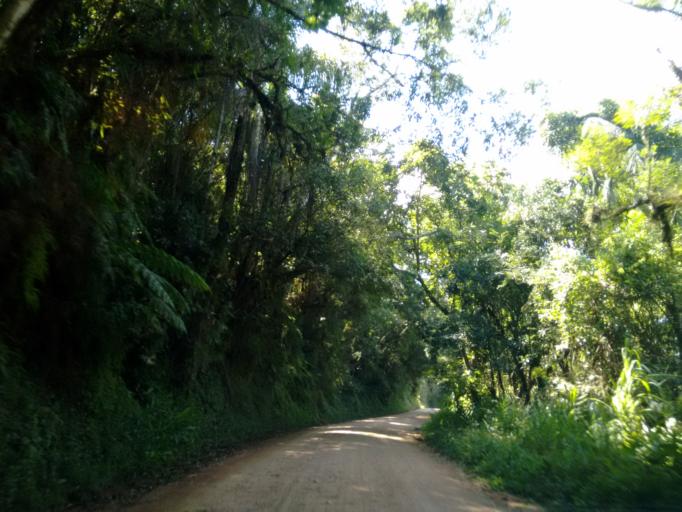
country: BR
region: Santa Catarina
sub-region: Indaial
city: Indaial
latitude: -26.9629
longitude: -49.1801
